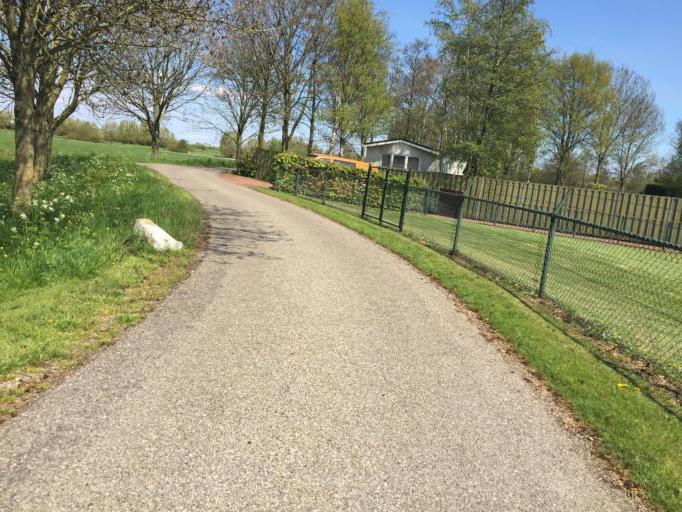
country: NL
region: North Holland
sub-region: Gemeente Aalsmeer
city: Aalsmeer
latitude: 52.2151
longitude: 4.7432
